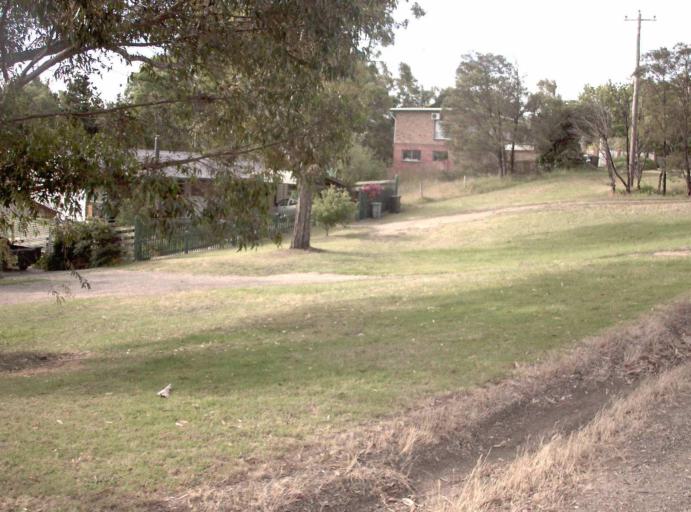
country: AU
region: Victoria
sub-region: Wellington
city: Heyfield
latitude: -37.9819
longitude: 146.7835
